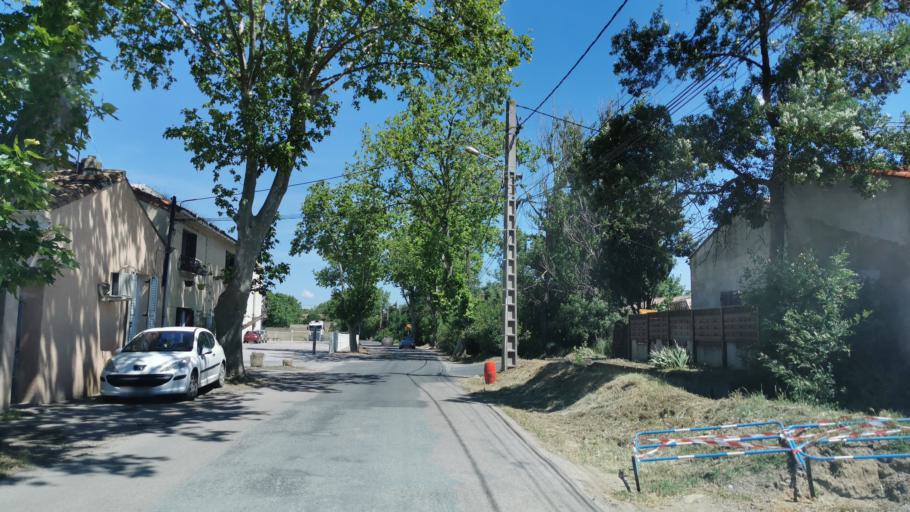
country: FR
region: Languedoc-Roussillon
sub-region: Departement de l'Aude
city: Canet
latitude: 43.2223
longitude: 2.8462
